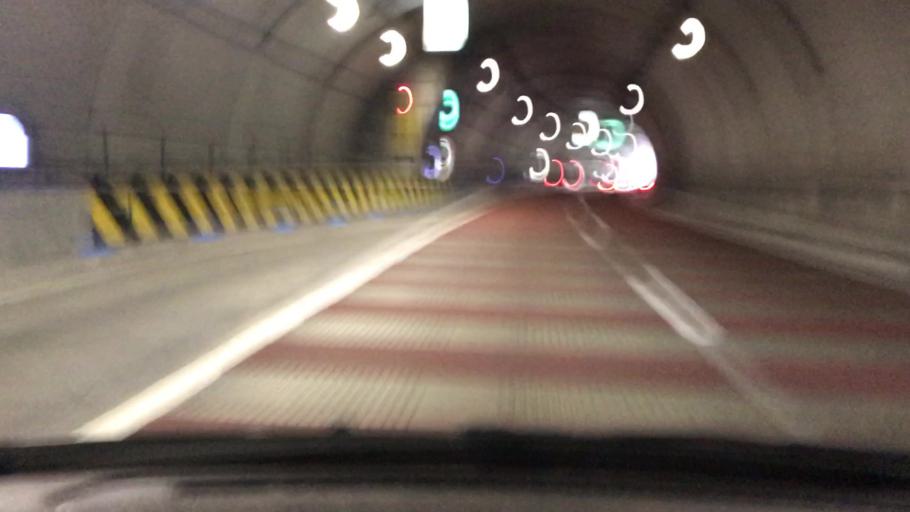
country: JP
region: Hyogo
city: Sandacho
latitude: 34.8280
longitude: 135.2576
